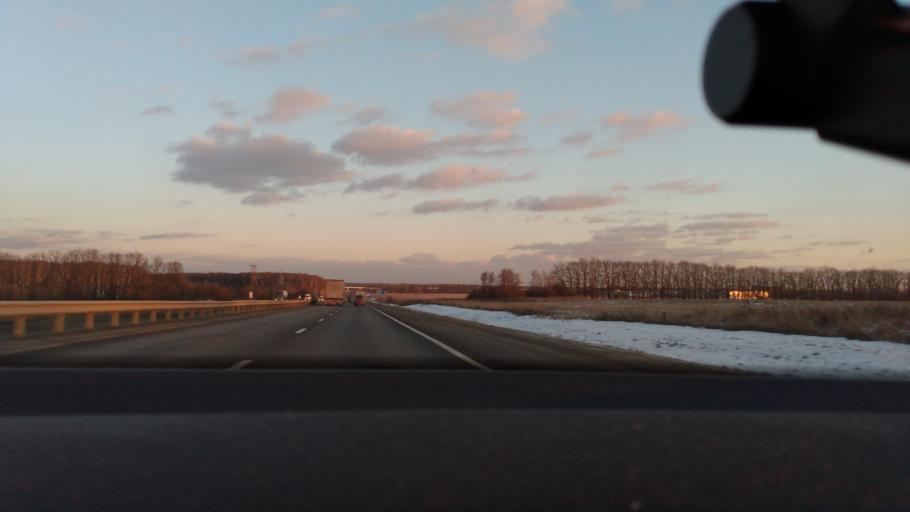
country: RU
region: Moskovskaya
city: Raduzhnyy
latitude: 55.1517
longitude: 38.7049
